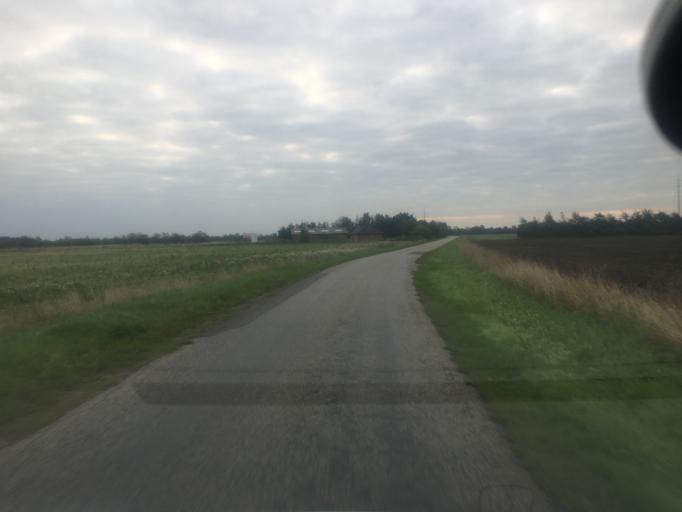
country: DK
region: South Denmark
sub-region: Tonder Kommune
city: Logumkloster
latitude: 55.0379
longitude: 8.9845
